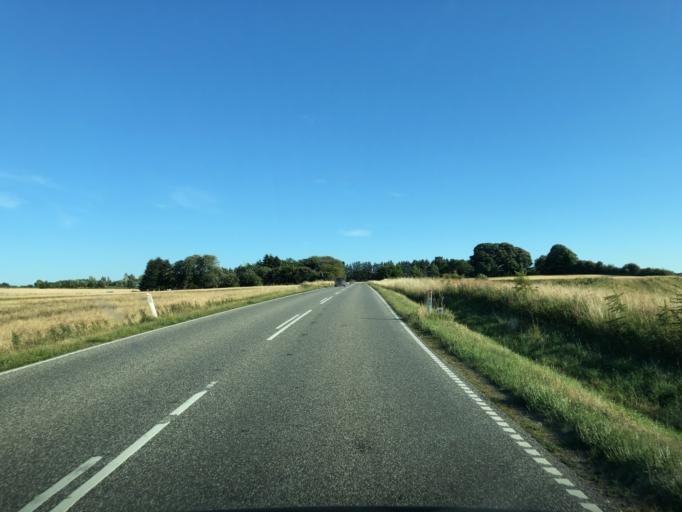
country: DK
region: Central Jutland
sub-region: Skanderborg Kommune
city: Stilling
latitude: 56.0858
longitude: 9.9714
